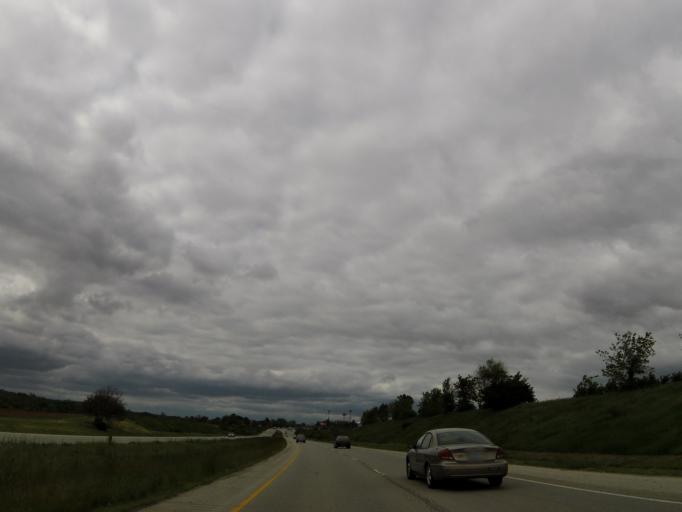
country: US
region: Kentucky
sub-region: Scott County
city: Georgetown
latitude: 38.2061
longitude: -84.5376
